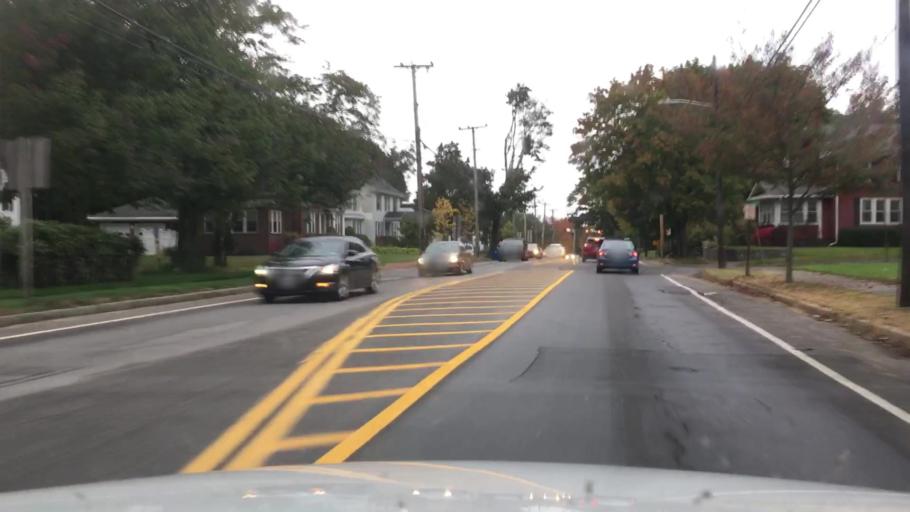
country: US
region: Maine
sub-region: Cumberland County
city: South Portland Gardens
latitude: 43.6660
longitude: -70.2935
